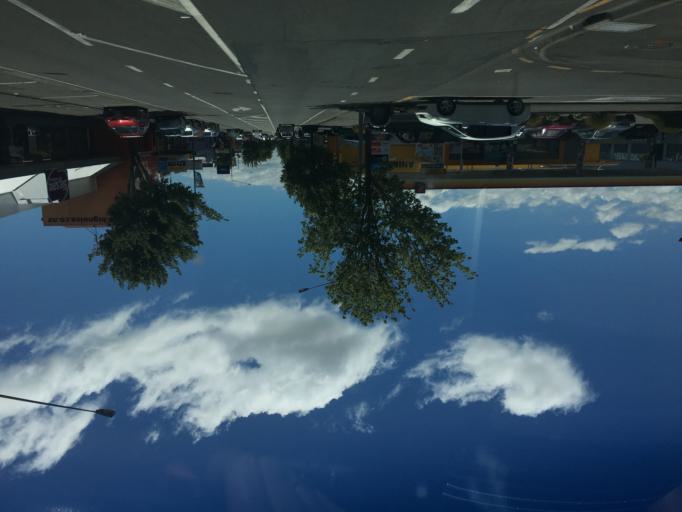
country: NZ
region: Hawke's Bay
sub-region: Hastings District
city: Hastings
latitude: -39.6381
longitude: 176.8392
